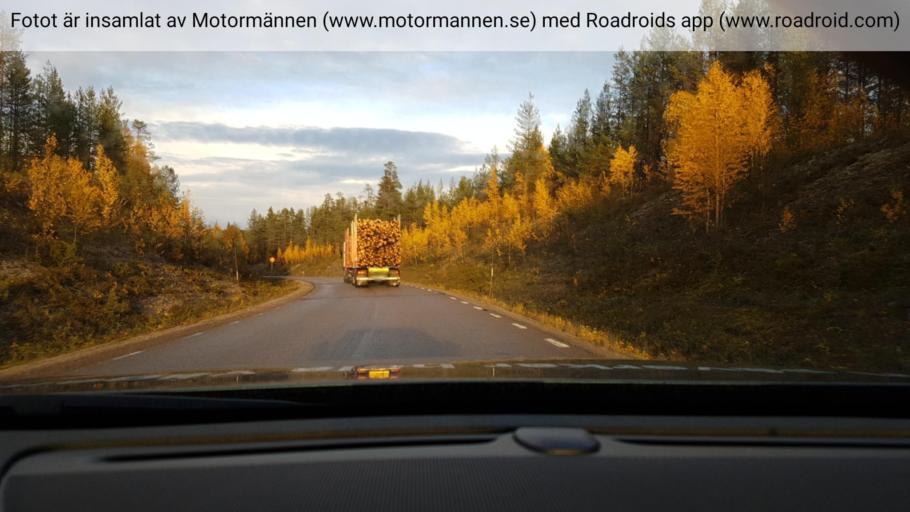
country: SE
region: Norrbotten
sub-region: Overkalix Kommun
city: OEverkalix
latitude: 66.6485
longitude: 22.7058
